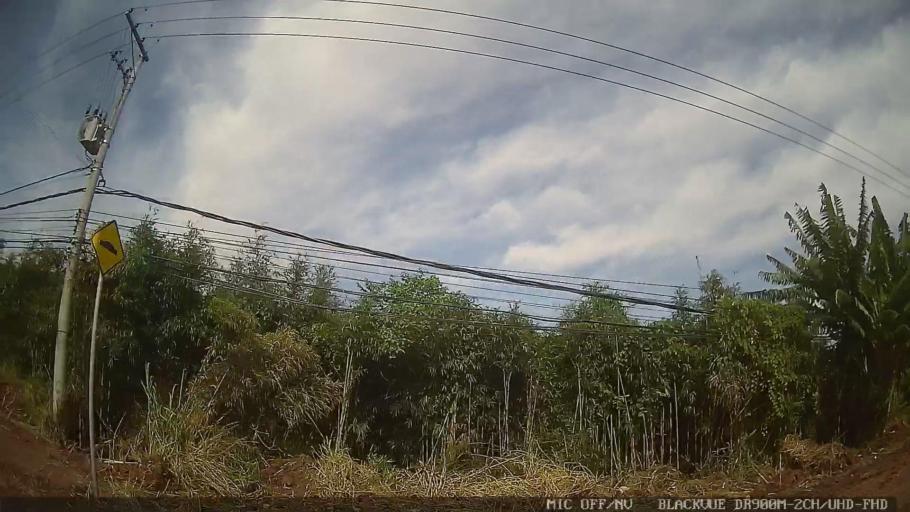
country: BR
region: Sao Paulo
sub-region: Itaquaquecetuba
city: Itaquaquecetuba
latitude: -23.4816
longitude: -46.2948
